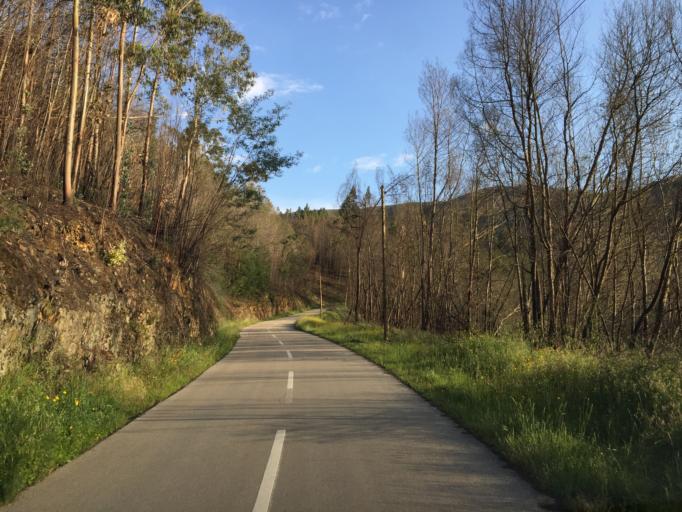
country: PT
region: Coimbra
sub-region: Arganil
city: Arganil
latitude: 40.1426
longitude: -8.0092
